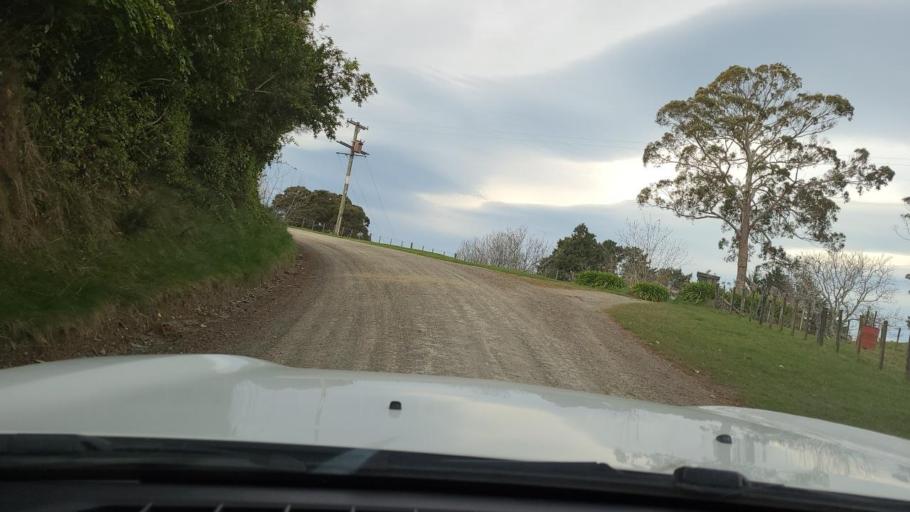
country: NZ
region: Hawke's Bay
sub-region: Napier City
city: Napier
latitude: -39.3002
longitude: 176.8330
